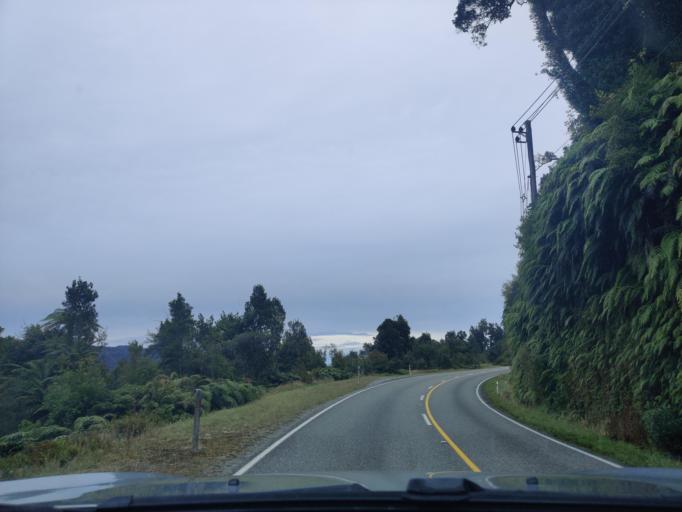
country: NZ
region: West Coast
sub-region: Westland District
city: Hokitika
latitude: -43.3263
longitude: 170.2143
